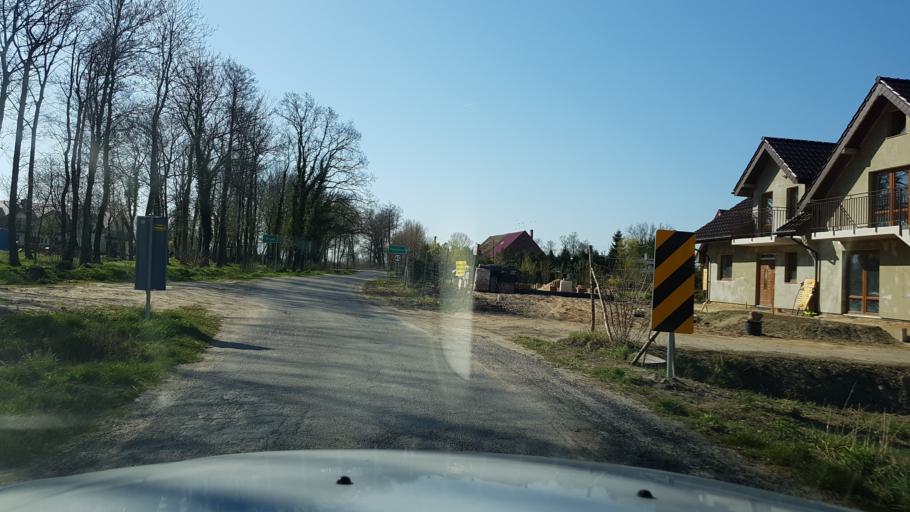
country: PL
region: West Pomeranian Voivodeship
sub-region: Powiat kolobrzeski
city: Ustronie Morskie
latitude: 54.2383
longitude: 15.8737
